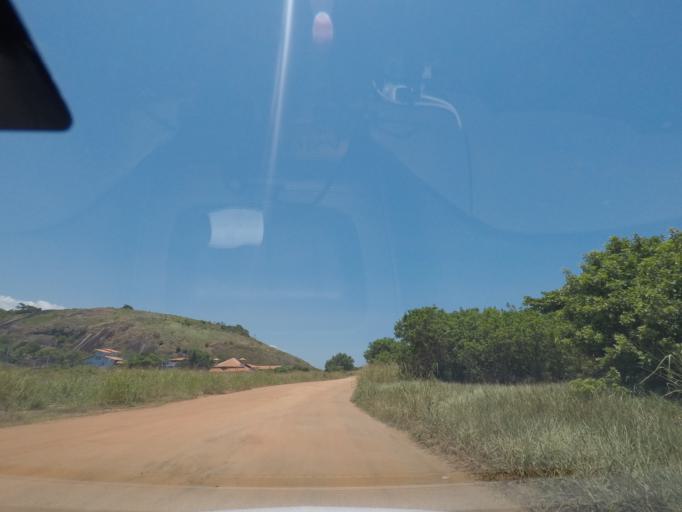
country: BR
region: Rio de Janeiro
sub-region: Niteroi
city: Niteroi
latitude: -22.9687
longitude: -43.0037
